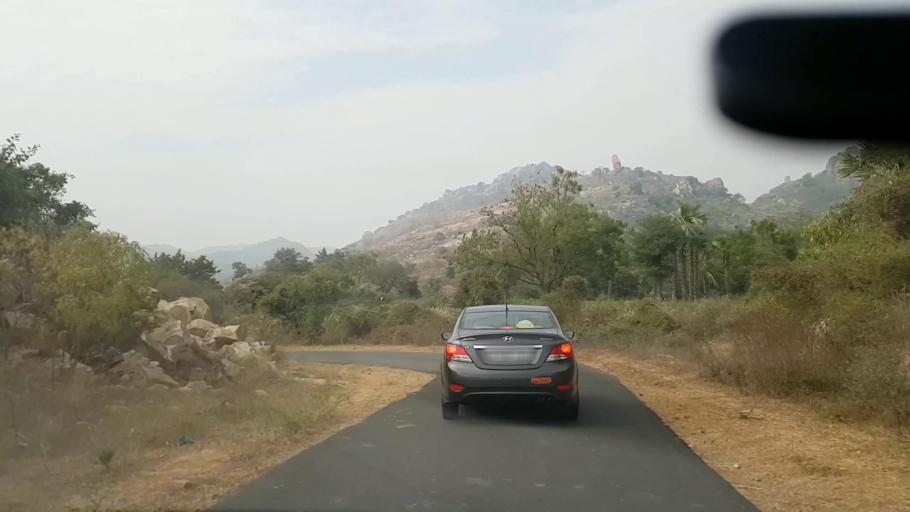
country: IN
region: Telangana
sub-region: Rangareddi
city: Ghatkesar
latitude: 17.1815
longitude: 78.8223
